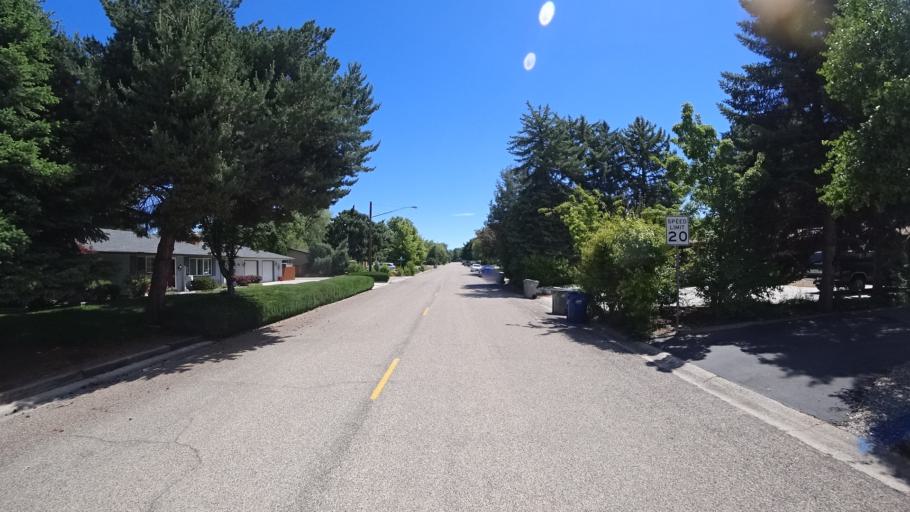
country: US
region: Idaho
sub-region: Ada County
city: Garden City
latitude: 43.5756
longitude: -116.2329
